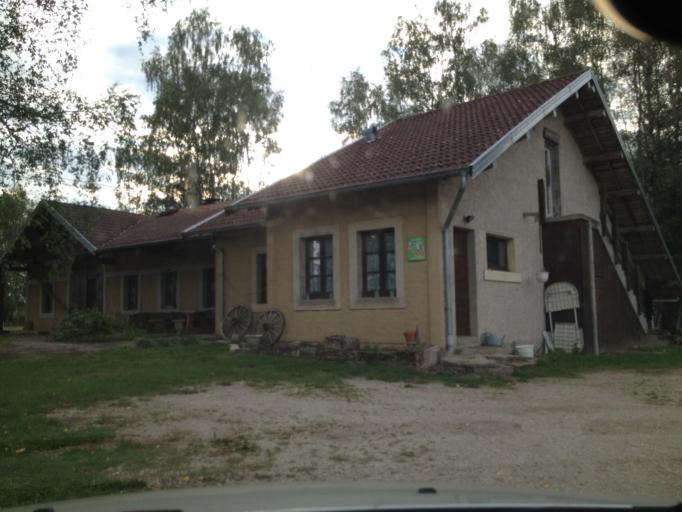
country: FR
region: Lorraine
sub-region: Departement des Vosges
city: Bains-les-Bains
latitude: 47.9956
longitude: 6.2108
